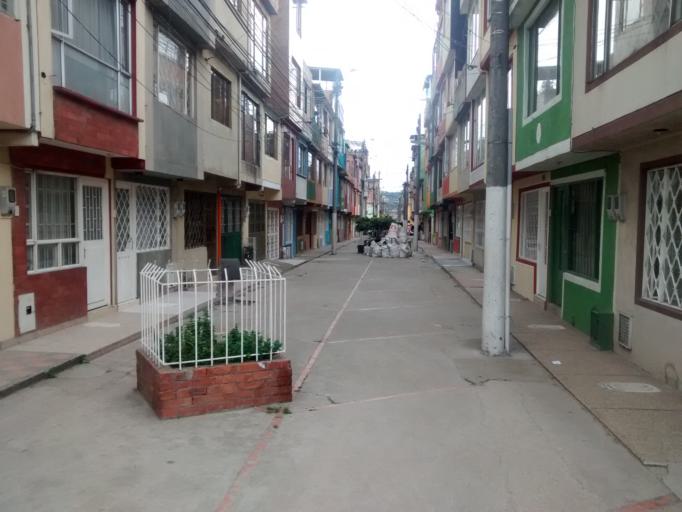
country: CO
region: Cundinamarca
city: Cota
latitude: 4.7193
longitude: -74.1028
